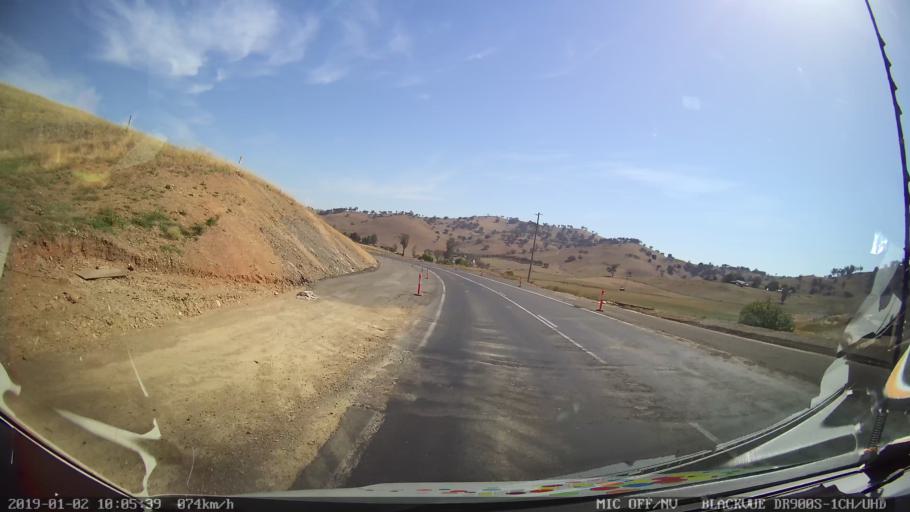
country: AU
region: New South Wales
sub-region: Gundagai
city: Gundagai
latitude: -35.1572
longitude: 148.1180
